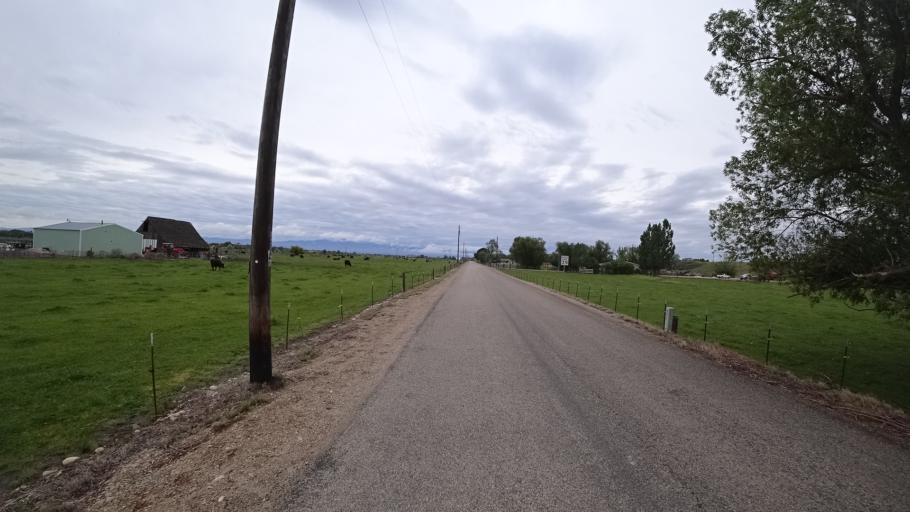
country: US
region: Idaho
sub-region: Ada County
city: Star
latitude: 43.6705
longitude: -116.4926
